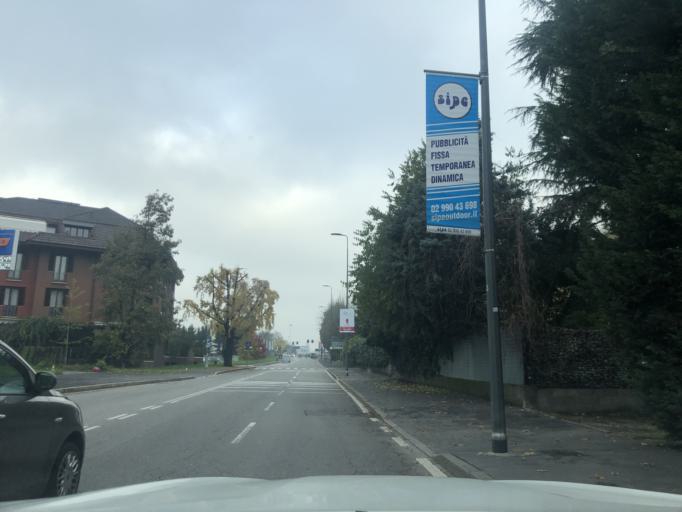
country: IT
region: Lombardy
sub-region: Citta metropolitana di Milano
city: Baranzate
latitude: 45.4852
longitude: 9.1303
